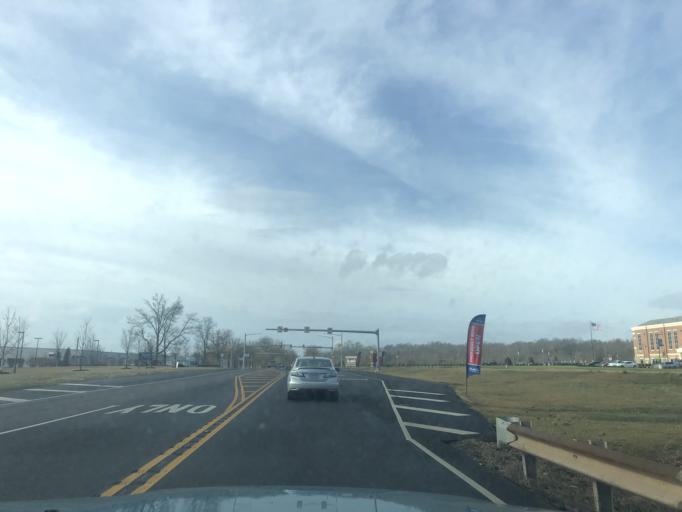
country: US
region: Pennsylvania
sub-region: Bucks County
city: Quakertown
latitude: 40.4434
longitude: -75.3733
